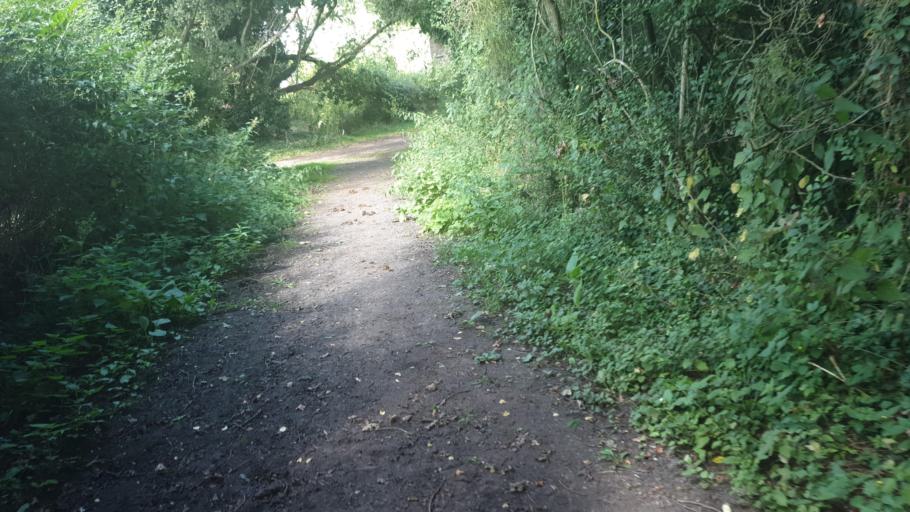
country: GB
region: England
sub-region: Suffolk
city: Shotley Gate
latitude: 51.9231
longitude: 1.2158
